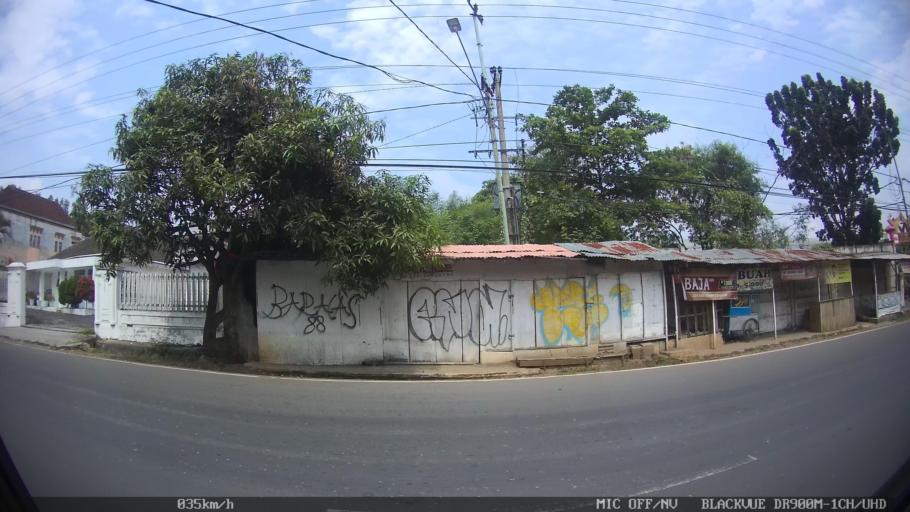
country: ID
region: Lampung
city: Bandarlampung
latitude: -5.4140
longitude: 105.2467
